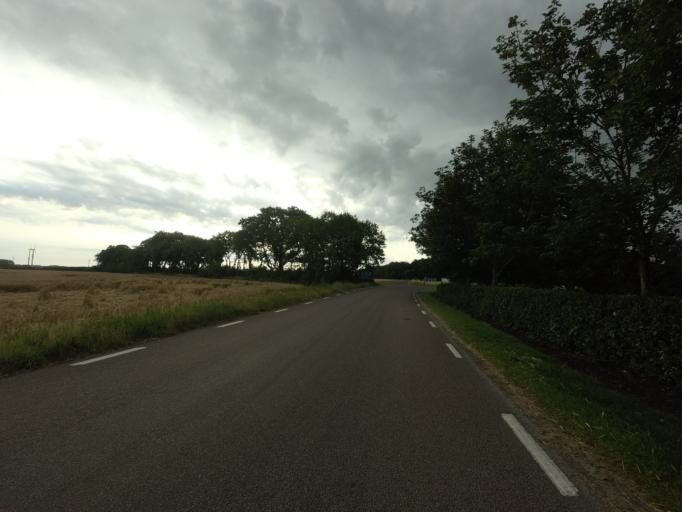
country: SE
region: Skane
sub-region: Helsingborg
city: Odakra
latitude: 56.1528
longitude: 12.7304
